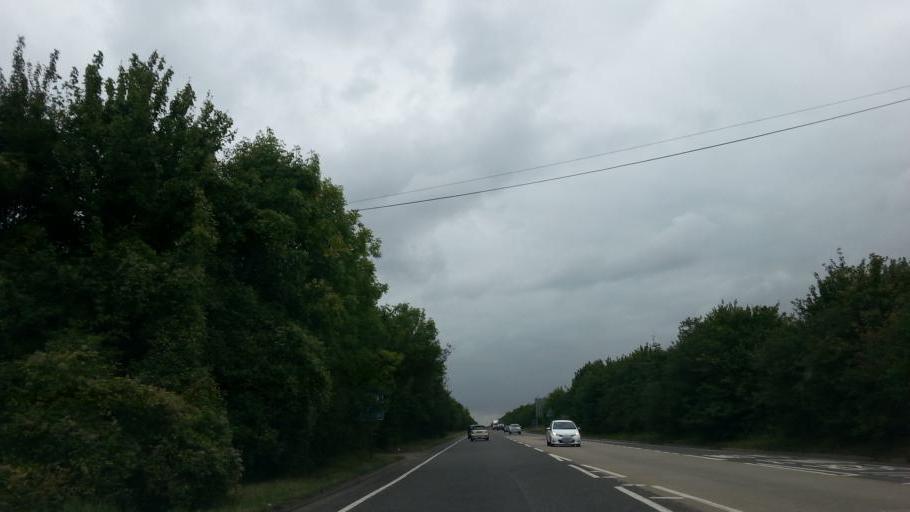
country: GB
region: England
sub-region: Essex
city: Chelmsford
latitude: 51.7780
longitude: 0.4878
